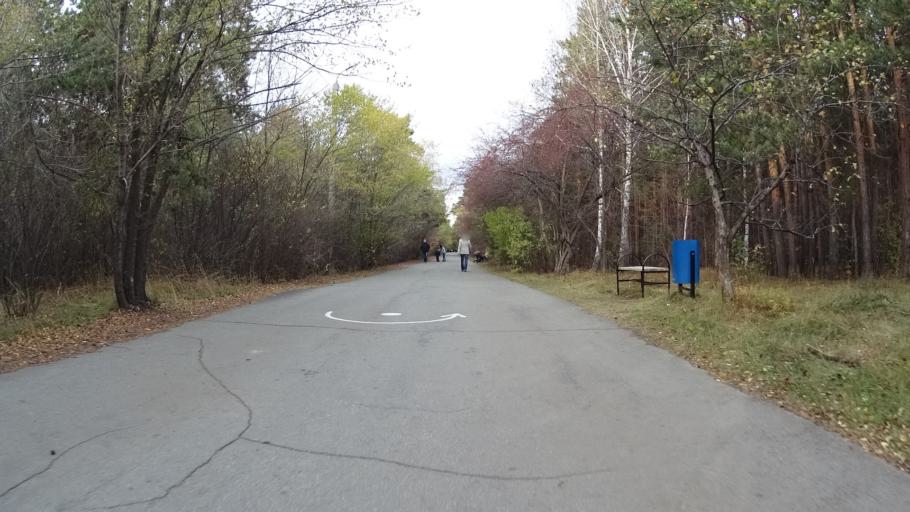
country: RU
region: Chelyabinsk
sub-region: Gorod Chelyabinsk
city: Chelyabinsk
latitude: 55.1495
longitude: 61.3560
